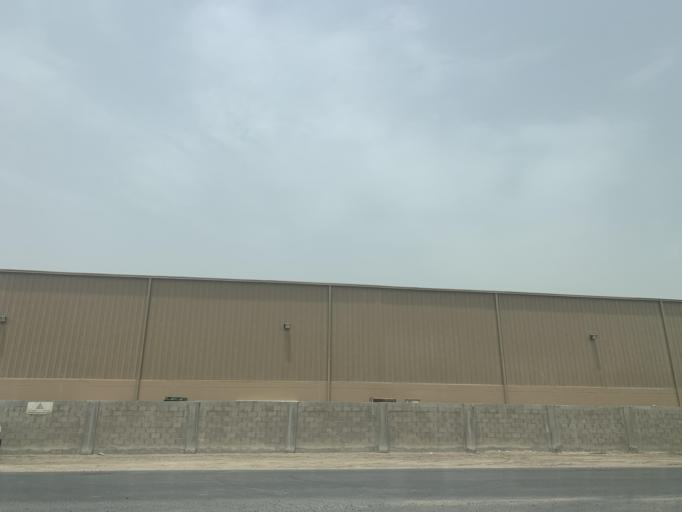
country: BH
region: Northern
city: Sitrah
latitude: 26.1773
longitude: 50.6217
